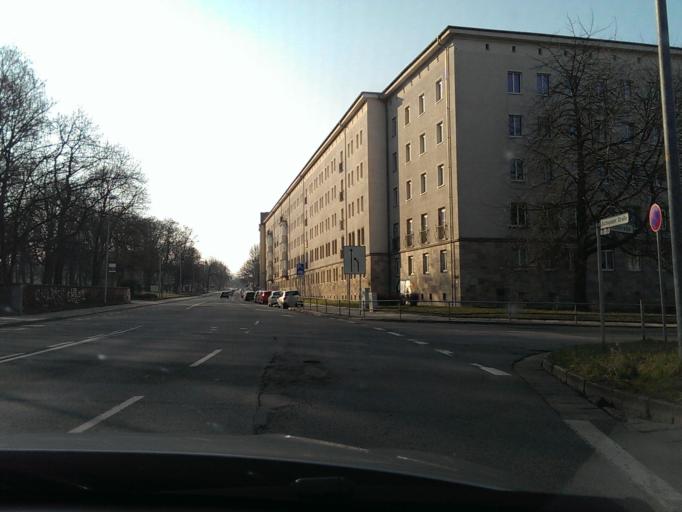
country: DE
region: Saxony
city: Chemnitz
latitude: 50.8315
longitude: 12.9252
